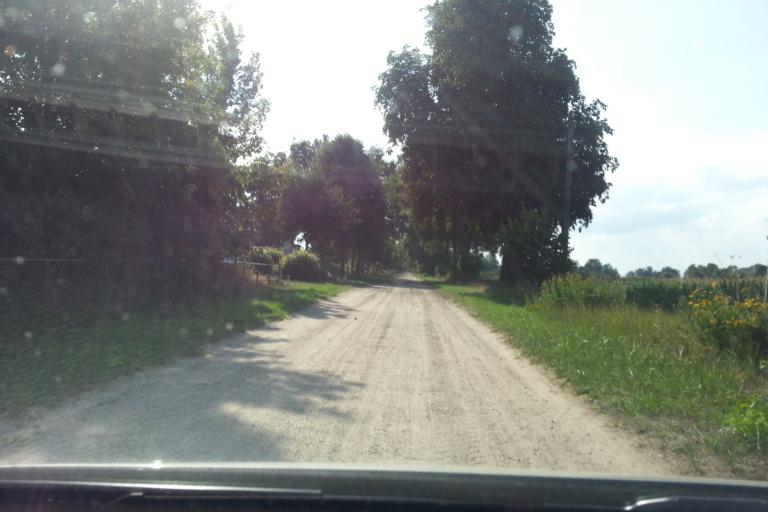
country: DE
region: Mecklenburg-Vorpommern
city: Ferdinandshof
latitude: 53.6425
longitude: 13.8440
